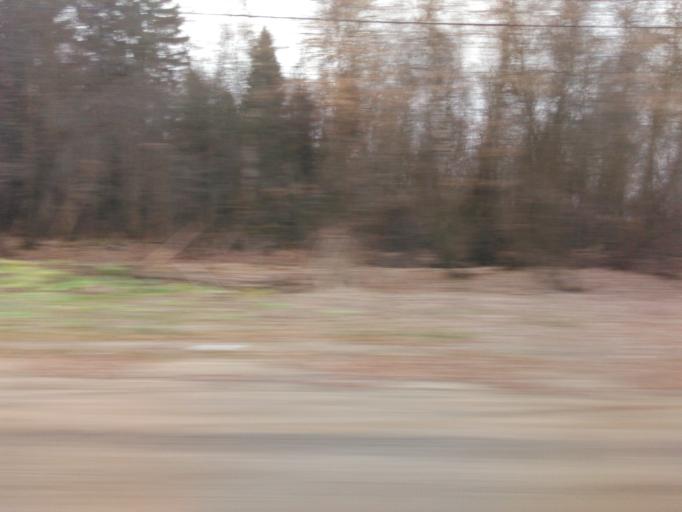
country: RU
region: Moskovskaya
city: Ashukino
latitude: 56.1447
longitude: 37.9882
